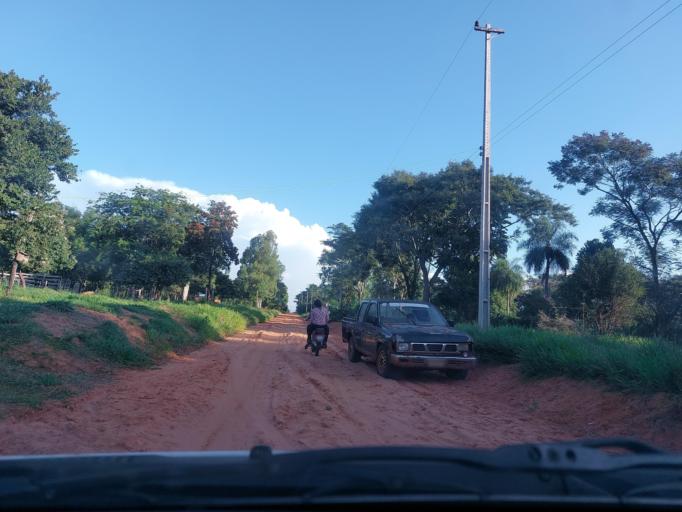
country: PY
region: San Pedro
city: Lima
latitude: -24.1531
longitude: -56.0392
